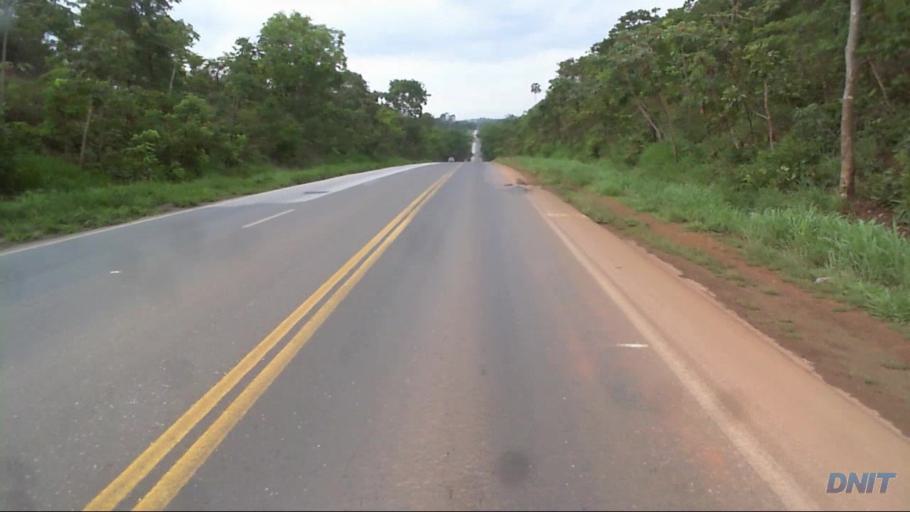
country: BR
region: Goias
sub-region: Uruacu
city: Uruacu
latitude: -14.5851
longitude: -49.1608
